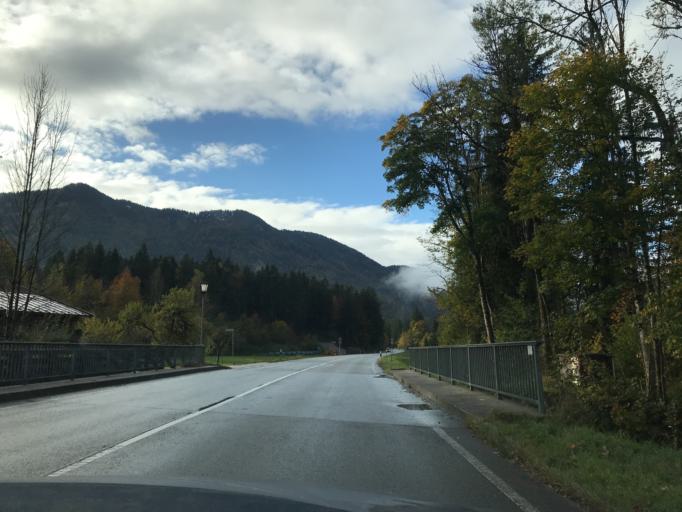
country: DE
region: Bavaria
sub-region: Upper Bavaria
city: Lenggries
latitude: 47.6345
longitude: 11.5945
